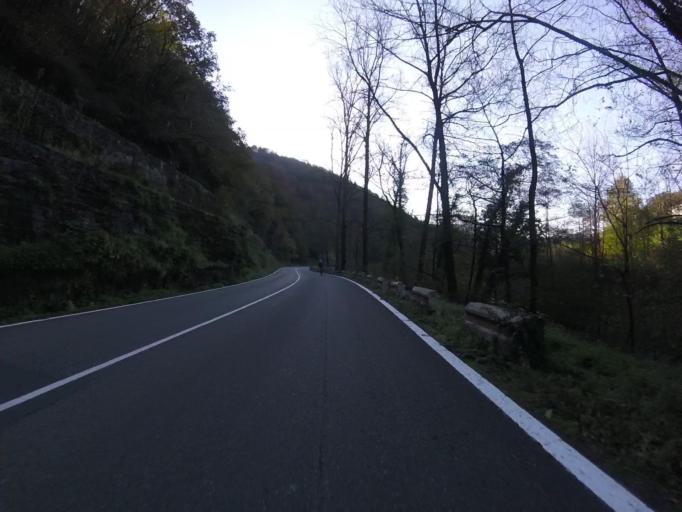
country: ES
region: Navarre
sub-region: Provincia de Navarra
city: Lesaka
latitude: 43.2476
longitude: -1.6701
